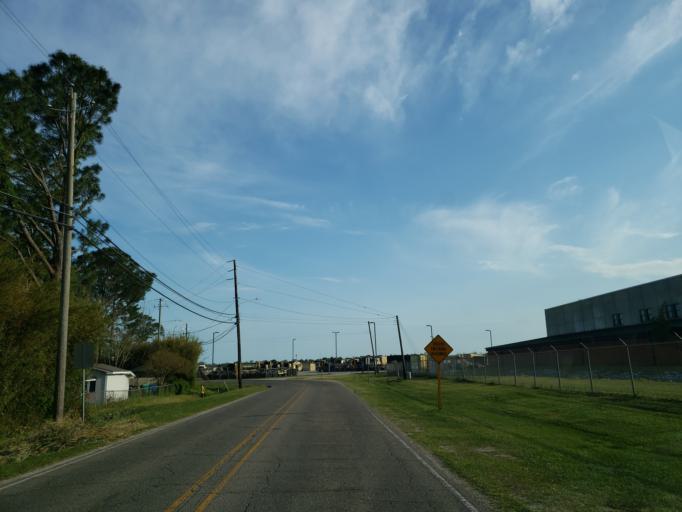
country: US
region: Mississippi
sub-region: Harrison County
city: West Gulfport
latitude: 30.4027
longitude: -89.0622
